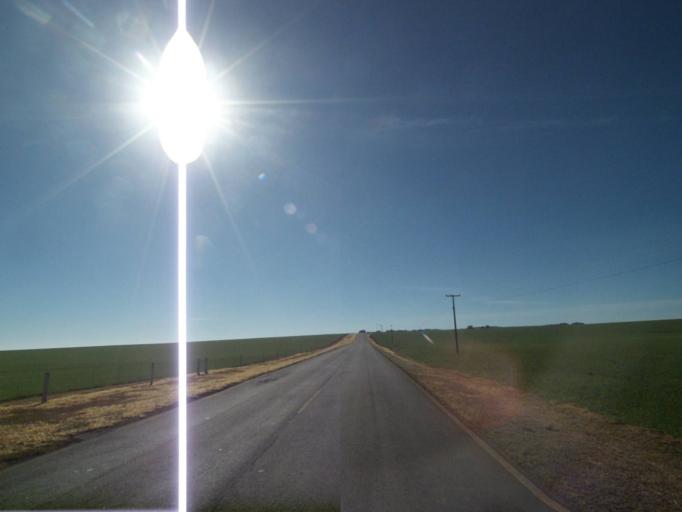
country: BR
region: Parana
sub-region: Tibagi
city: Tibagi
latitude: -24.5218
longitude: -50.3538
